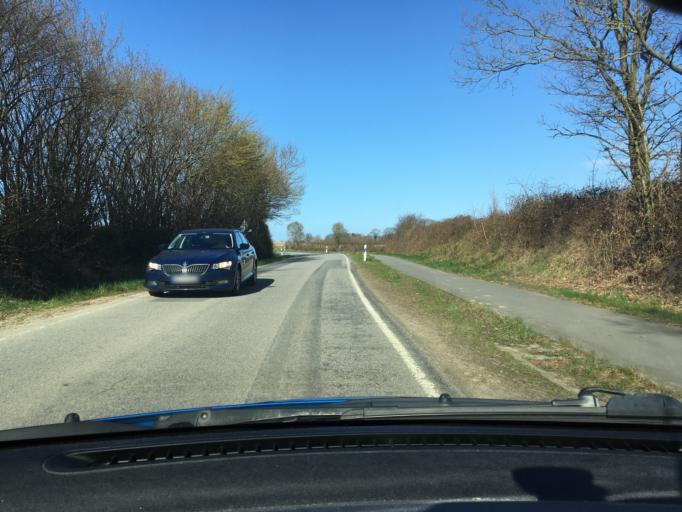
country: DE
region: Schleswig-Holstein
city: Fahrdorf
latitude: 54.5035
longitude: 9.6301
